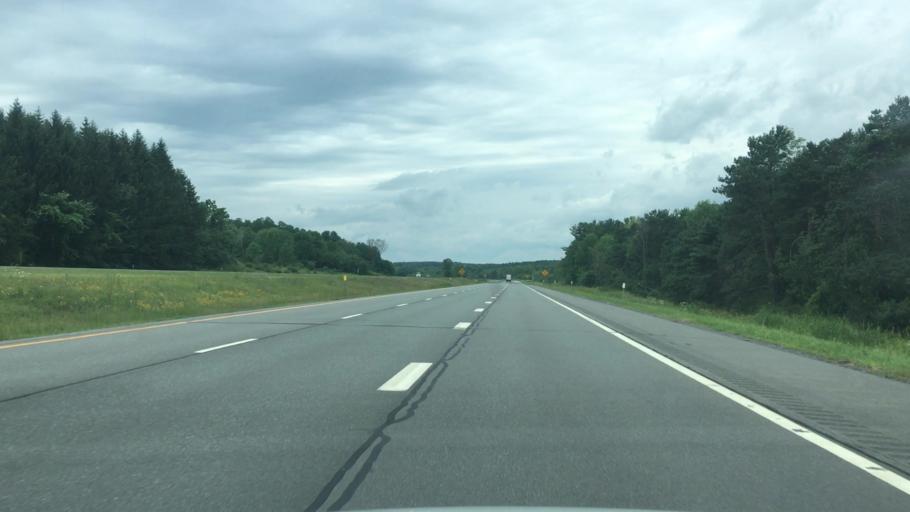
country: US
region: New York
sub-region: Schoharie County
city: Schoharie
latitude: 42.7241
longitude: -74.2314
